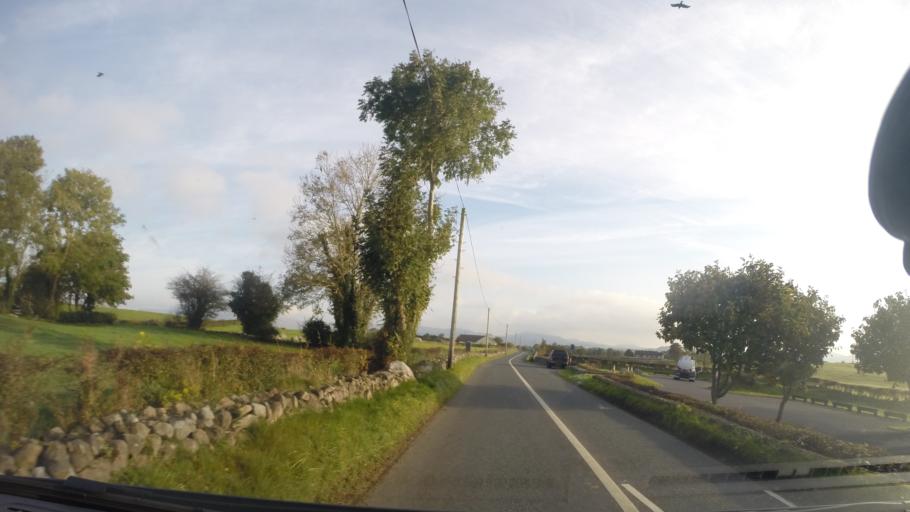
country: IE
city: Ballisodare
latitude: 54.2506
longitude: -8.5204
